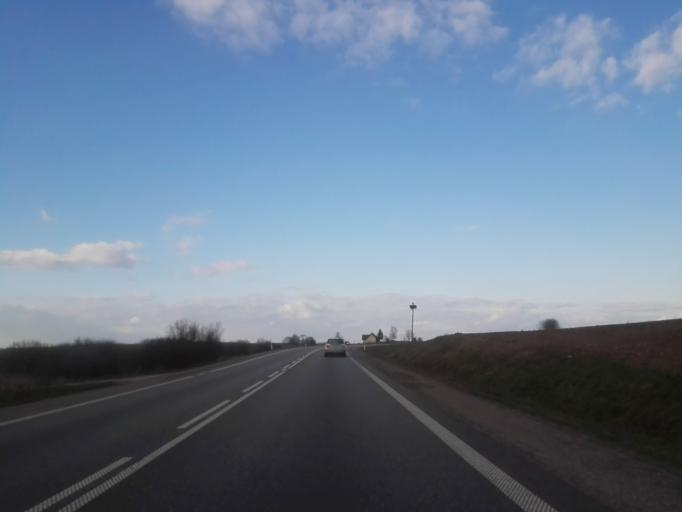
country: PL
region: Podlasie
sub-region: Suwalki
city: Suwalki
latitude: 54.2071
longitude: 23.0253
